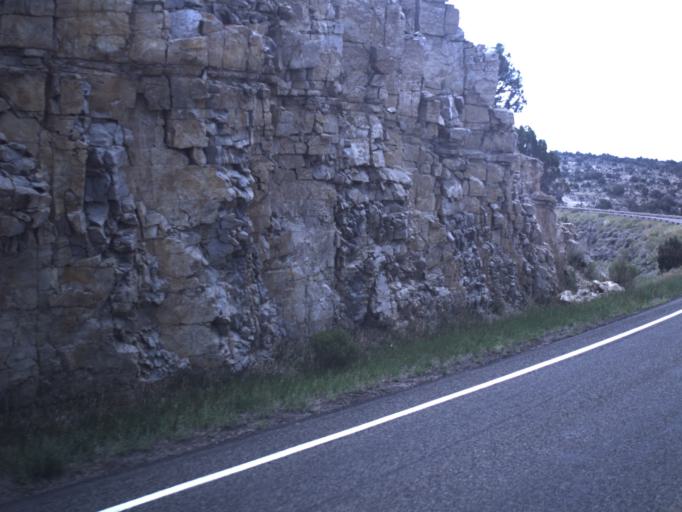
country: US
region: Utah
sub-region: Daggett County
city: Manila
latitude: 40.9414
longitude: -109.7134
